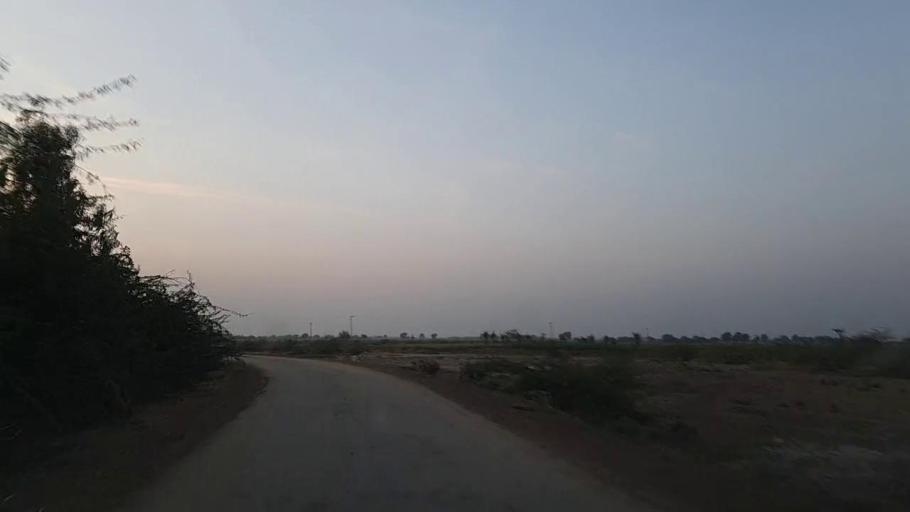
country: PK
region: Sindh
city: Naukot
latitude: 24.9844
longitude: 69.4254
